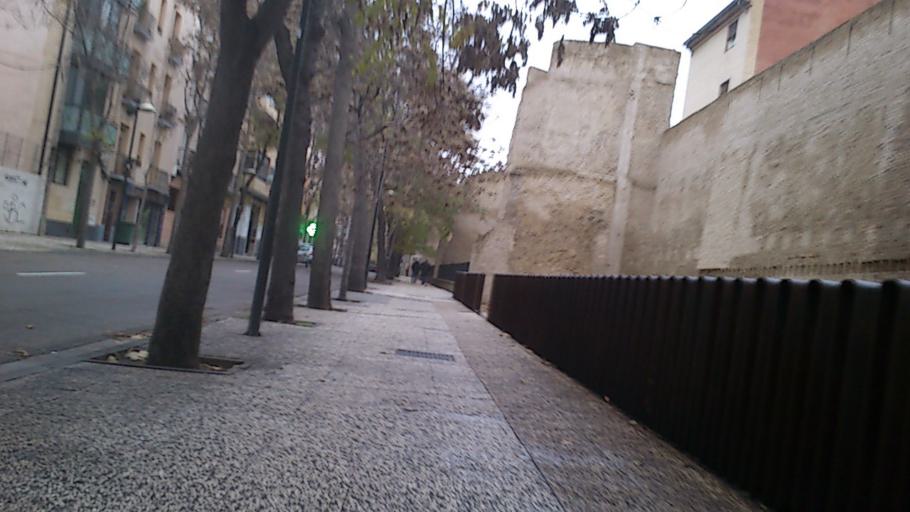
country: ES
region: Aragon
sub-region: Provincia de Zaragoza
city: Zaragoza
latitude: 41.6529
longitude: -0.8716
